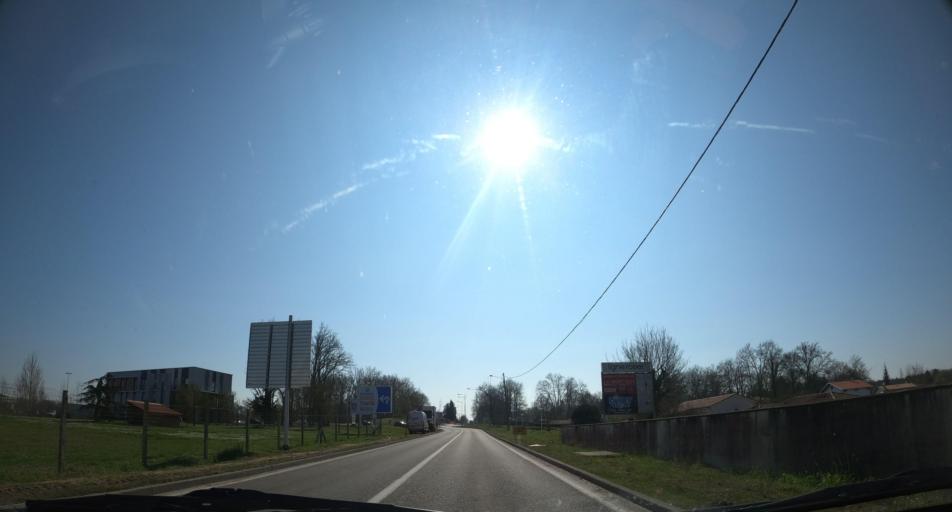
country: FR
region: Aquitaine
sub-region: Departement des Landes
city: Mont-de-Marsan
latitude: 43.8635
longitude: -0.4863
